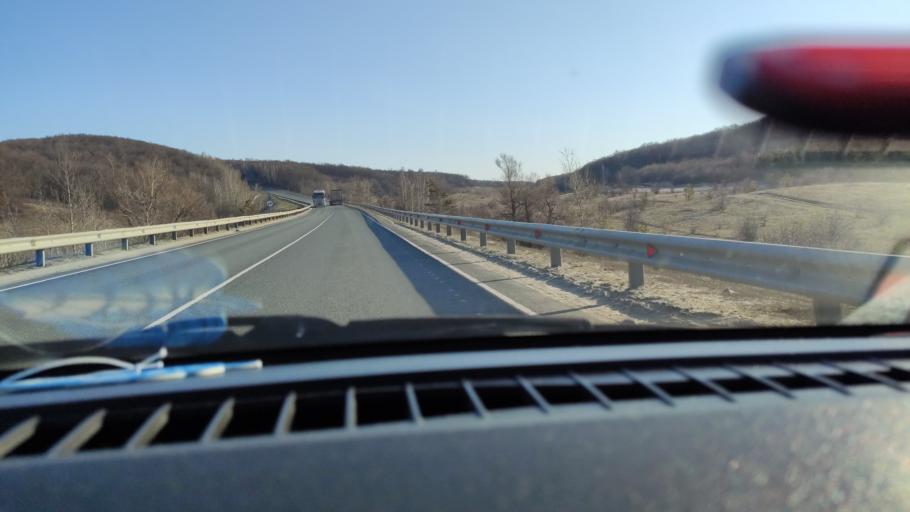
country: RU
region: Saratov
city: Alekseyevka
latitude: 52.4100
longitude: 48.0038
